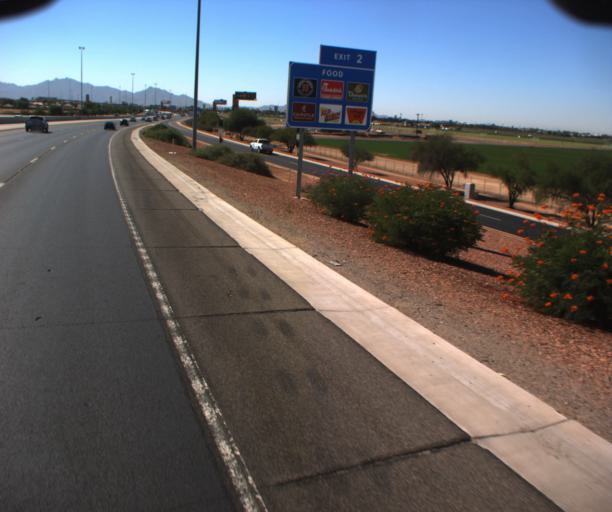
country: US
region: Arizona
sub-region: Maricopa County
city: Tolleson
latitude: 33.4775
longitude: -112.2646
